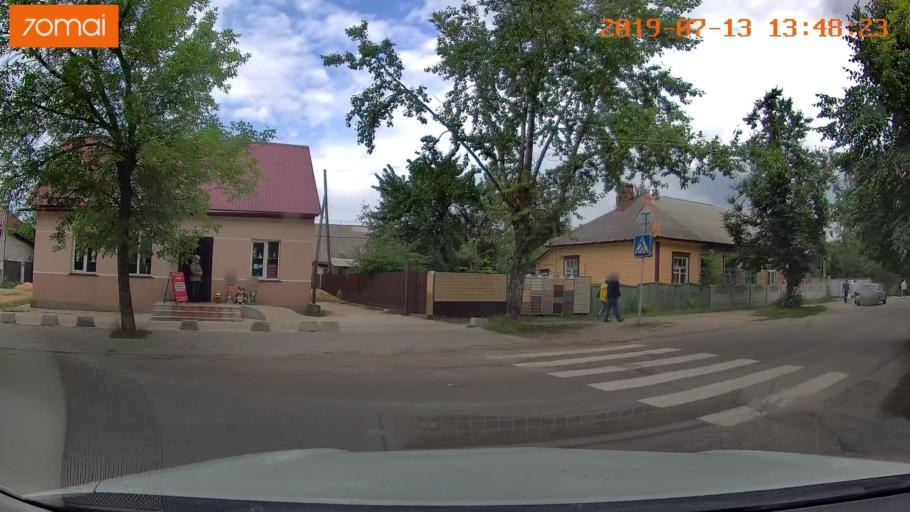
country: BY
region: Mogilev
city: Asipovichy
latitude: 53.2988
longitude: 28.6427
